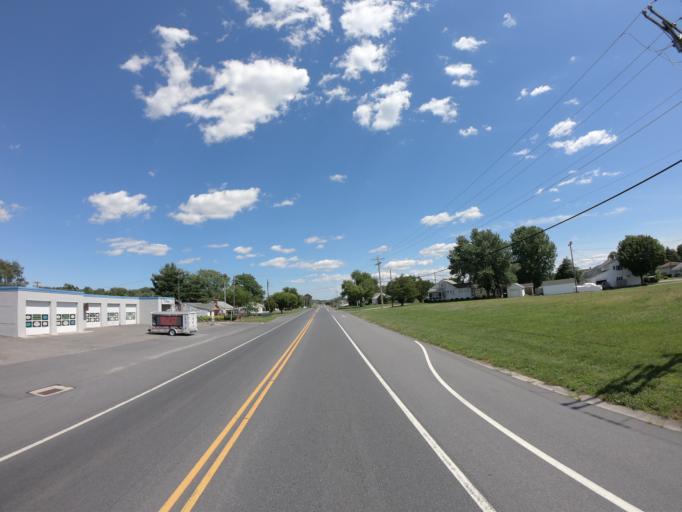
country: US
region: Delaware
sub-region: Sussex County
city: Milford
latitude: 38.9255
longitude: -75.4271
